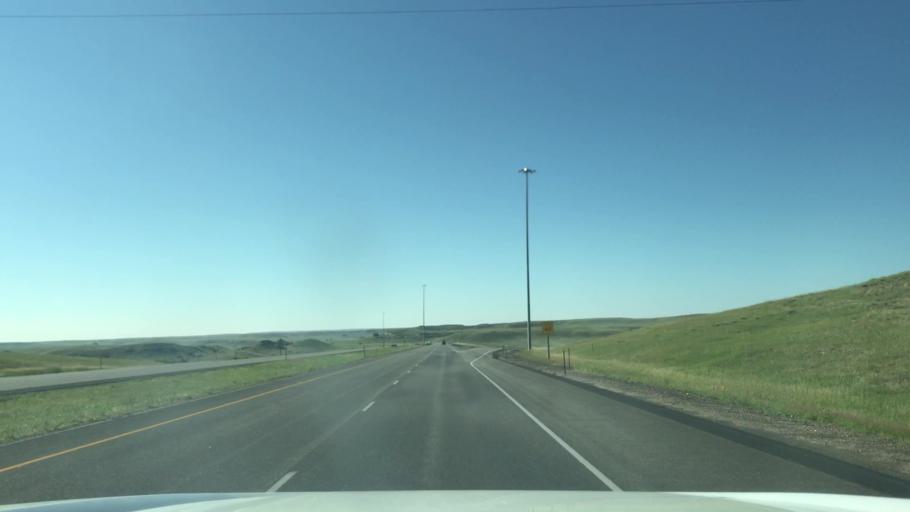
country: US
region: Wyoming
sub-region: Platte County
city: Wheatland
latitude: 41.9328
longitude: -104.9443
